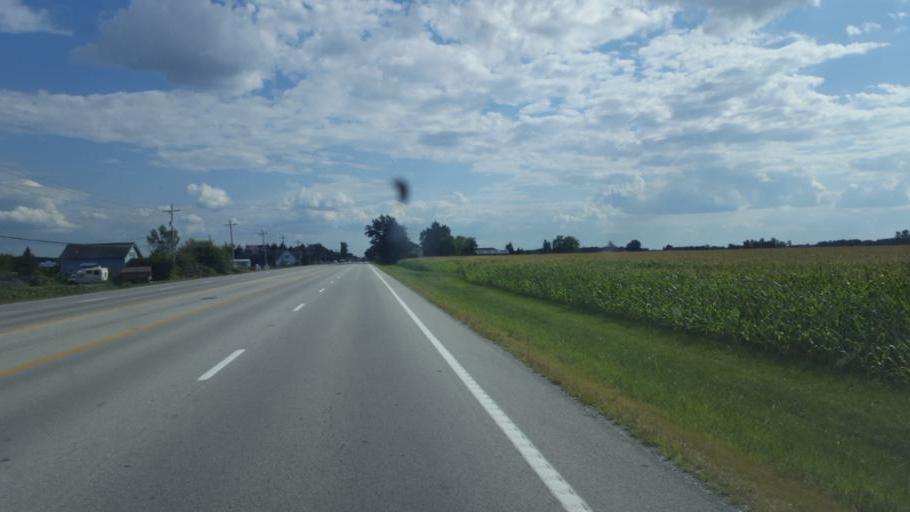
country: US
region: Ohio
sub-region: Wood County
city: Haskins
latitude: 41.4510
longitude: -83.6511
